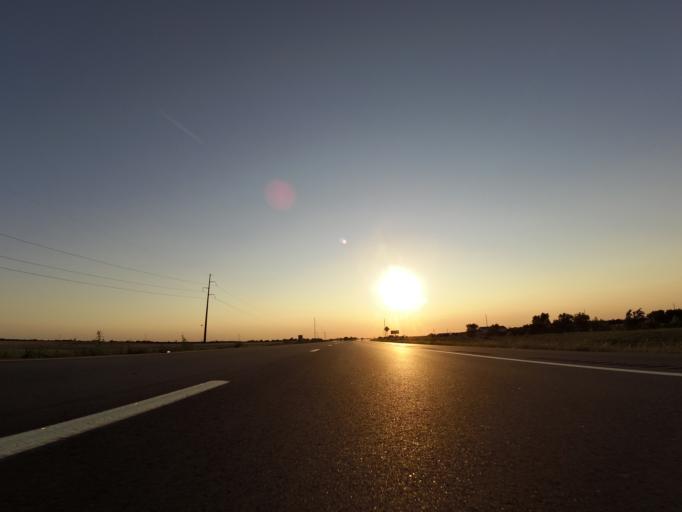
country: US
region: Kansas
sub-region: Reno County
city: South Hutchinson
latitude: 38.0134
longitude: -97.9720
